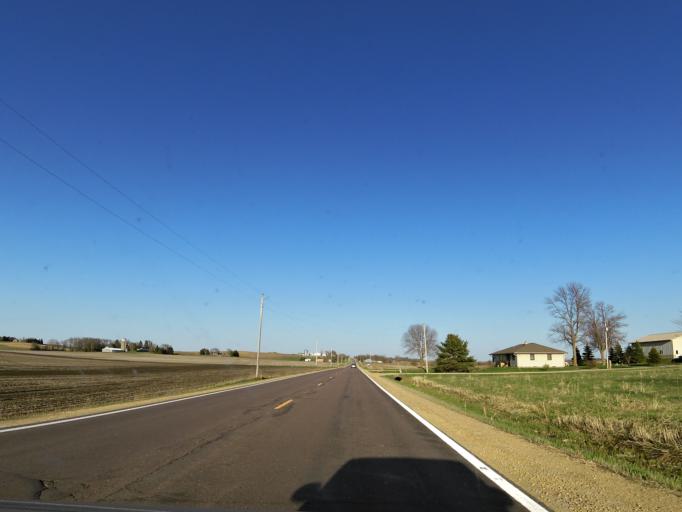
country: US
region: Minnesota
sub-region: Goodhue County
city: Cannon Falls
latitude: 44.6013
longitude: -92.9641
